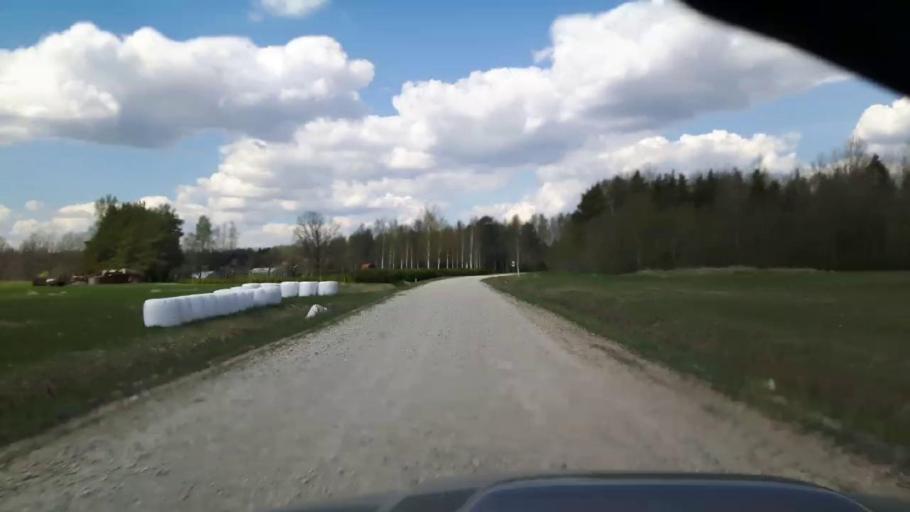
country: EE
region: Paernumaa
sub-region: Tootsi vald
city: Tootsi
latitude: 58.4642
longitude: 24.8654
